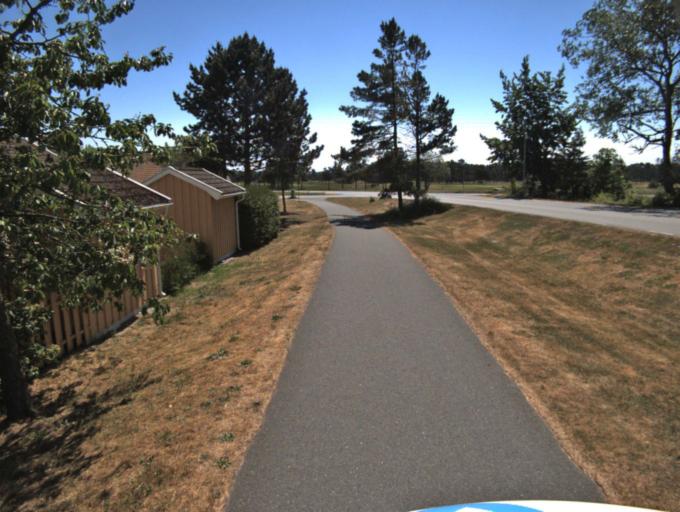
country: SE
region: Skane
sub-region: Kristianstads Kommun
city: Ahus
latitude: 55.9279
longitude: 14.2797
